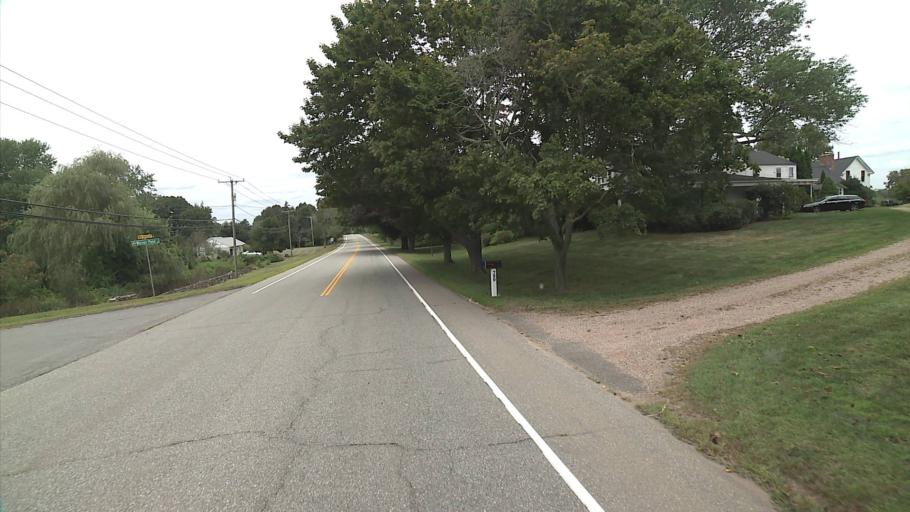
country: US
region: Connecticut
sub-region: Tolland County
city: Hebron
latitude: 41.6824
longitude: -72.4151
